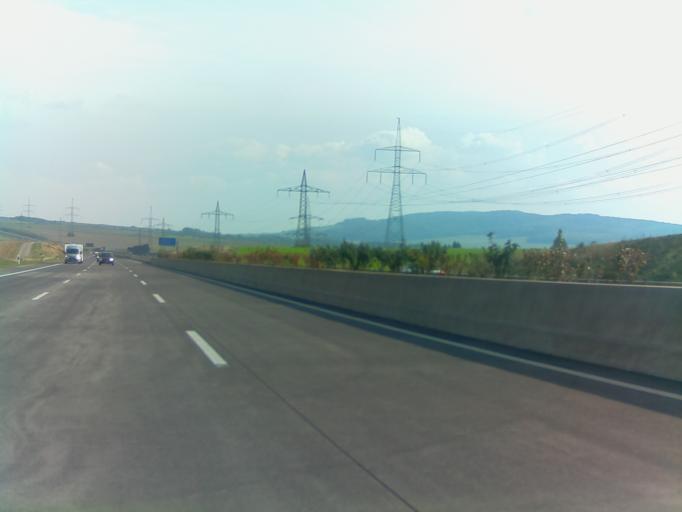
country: DE
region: Thuringia
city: Bischofroda
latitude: 51.0030
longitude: 10.4017
